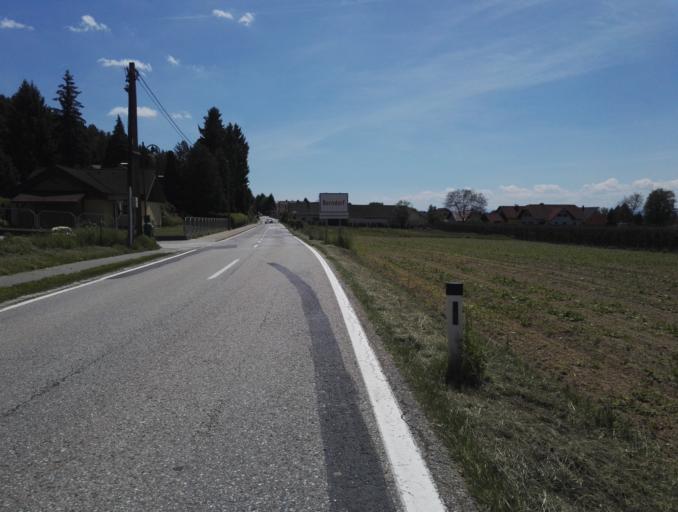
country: AT
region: Styria
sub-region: Politischer Bezirk Graz-Umgebung
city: Grambach
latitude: 47.0064
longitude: 15.5032
